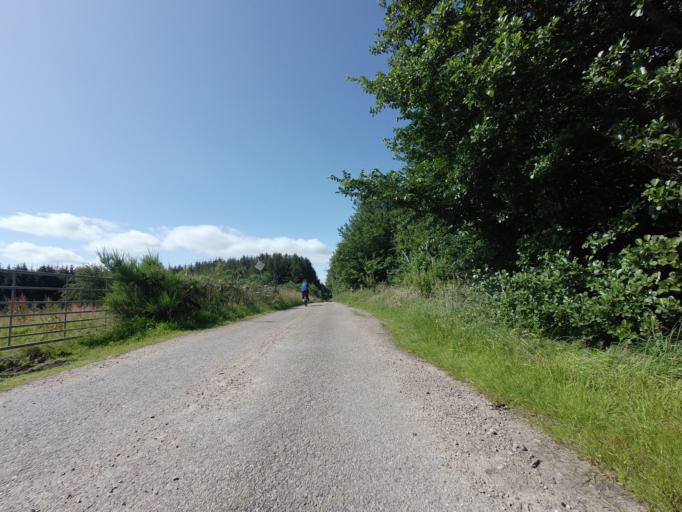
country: GB
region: Scotland
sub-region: Highland
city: Nairn
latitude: 57.5108
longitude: -3.8910
